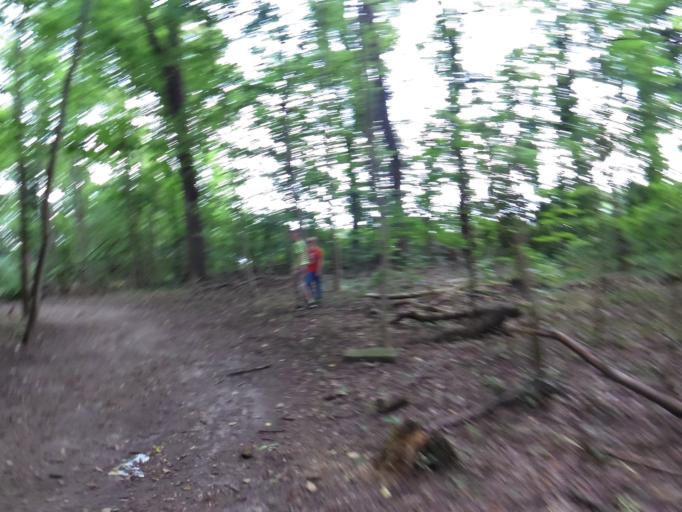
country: DE
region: Saxony
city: Leipzig
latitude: 51.3240
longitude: 12.4281
